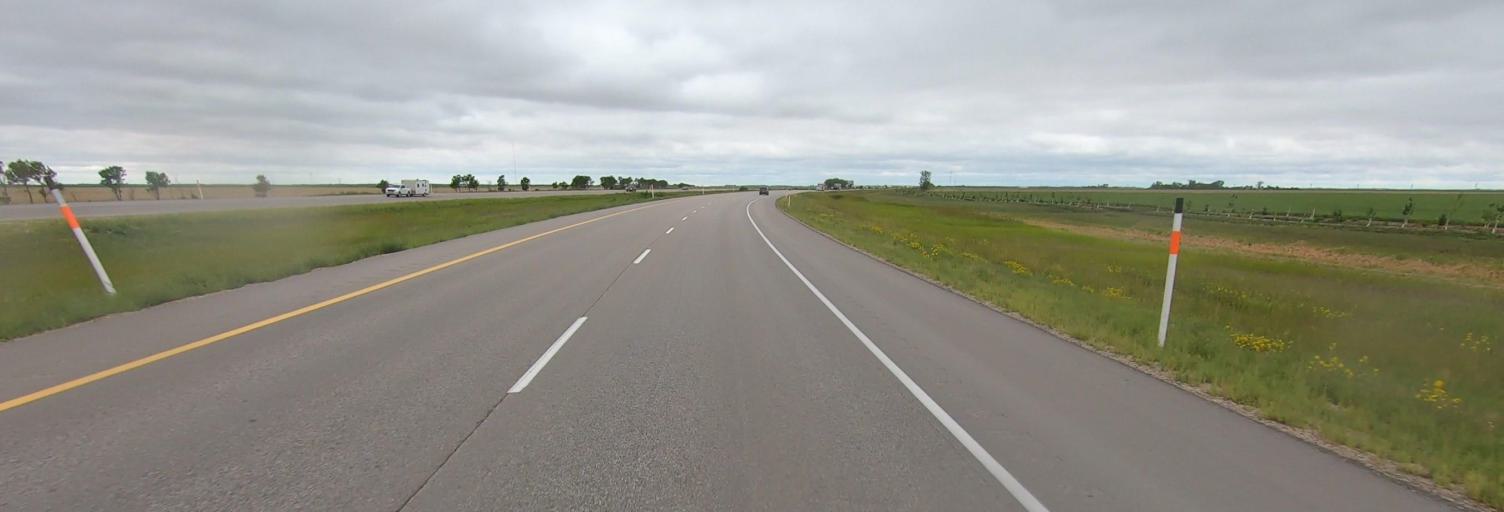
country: CA
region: Manitoba
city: Headingley
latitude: 49.8871
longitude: -97.6482
